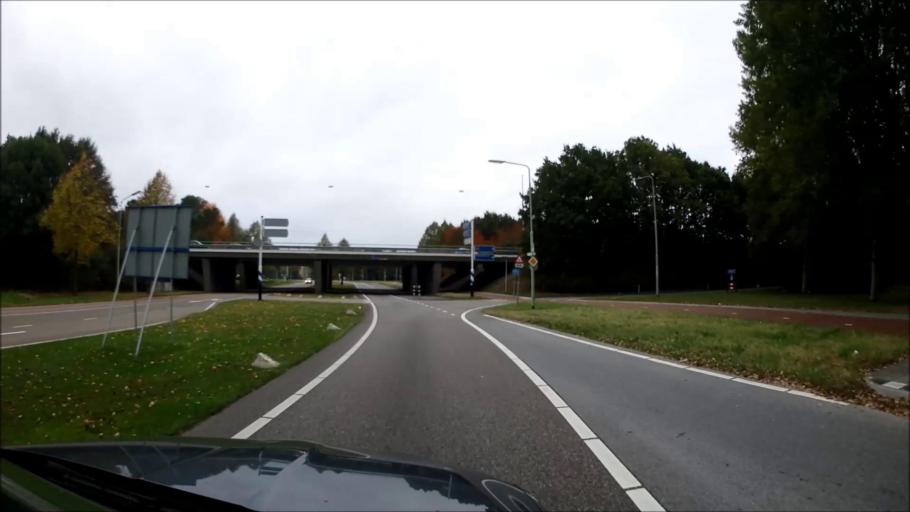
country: NL
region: North Holland
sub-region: Gemeente Naarden
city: Naarden
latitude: 52.3051
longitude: 5.1444
